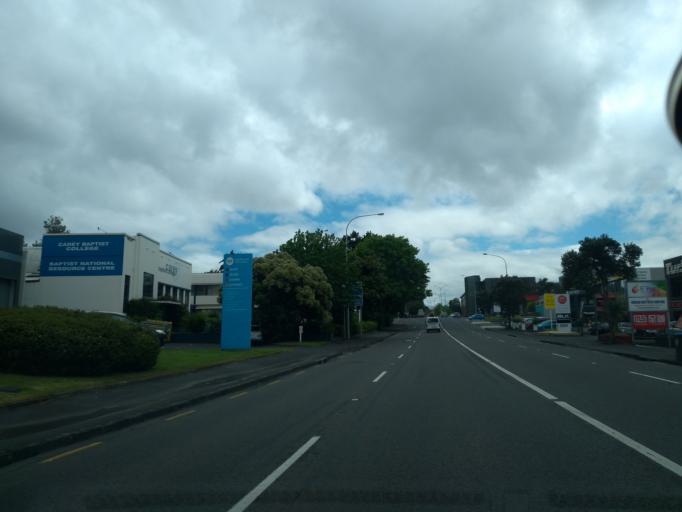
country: NZ
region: Auckland
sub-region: Auckland
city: Tamaki
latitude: -36.9048
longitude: 174.8095
